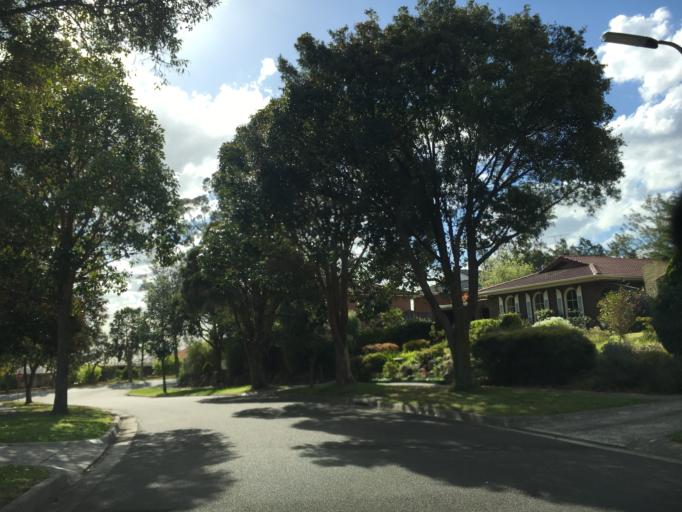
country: AU
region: Victoria
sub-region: Monash
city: Notting Hill
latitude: -37.8919
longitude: 145.1708
